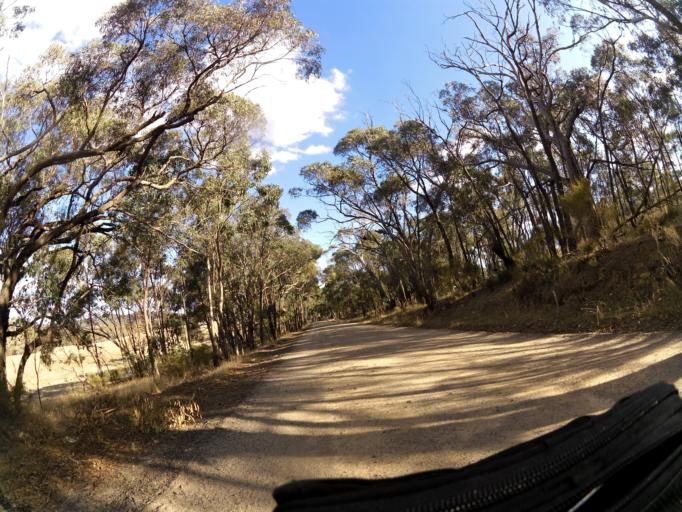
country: AU
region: Victoria
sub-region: Greater Bendigo
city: Kennington
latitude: -37.0153
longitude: 144.8078
